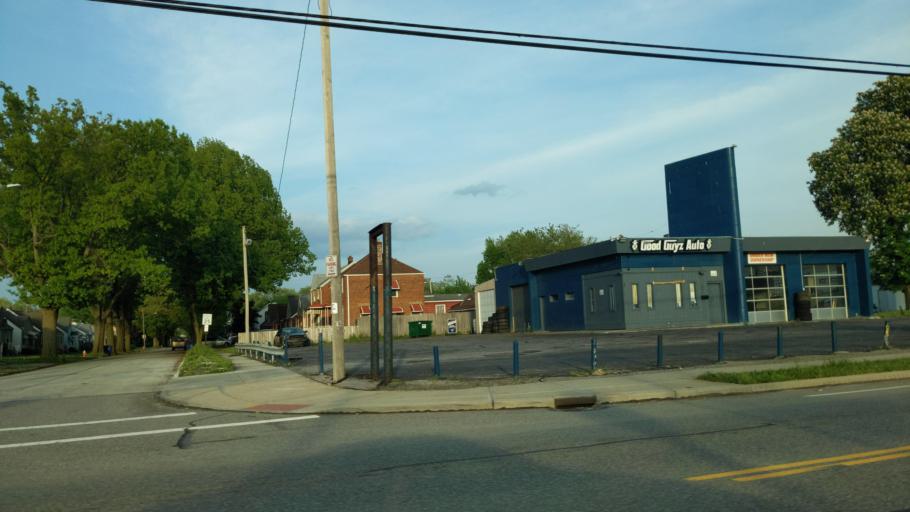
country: US
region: Ohio
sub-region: Cuyahoga County
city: Brook Park
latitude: 41.4251
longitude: -81.7804
